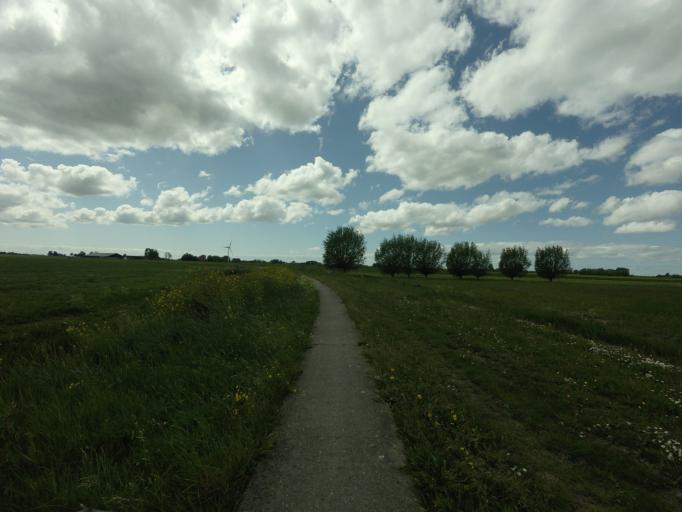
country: NL
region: Friesland
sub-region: Gemeente Franekeradeel
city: Tzum
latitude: 53.1298
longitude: 5.5663
